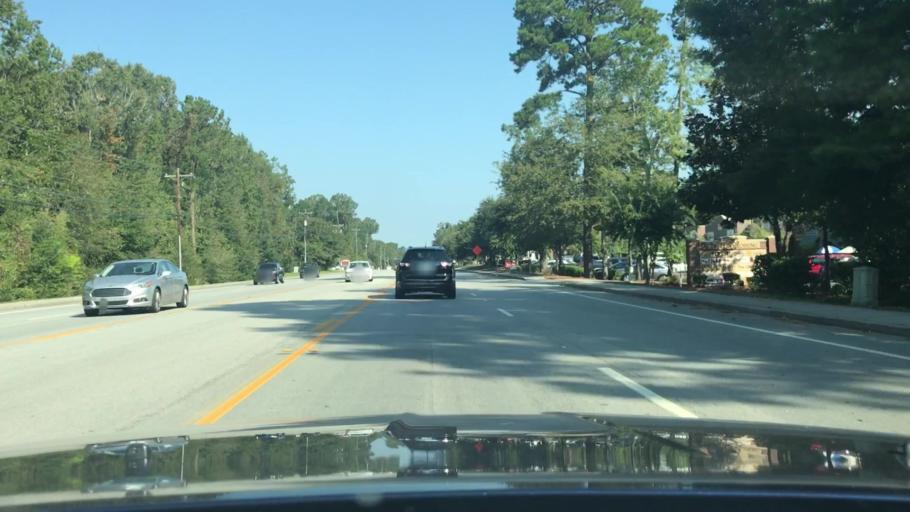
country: US
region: South Carolina
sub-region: Dorchester County
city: Centerville
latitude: 32.9739
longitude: -80.1710
